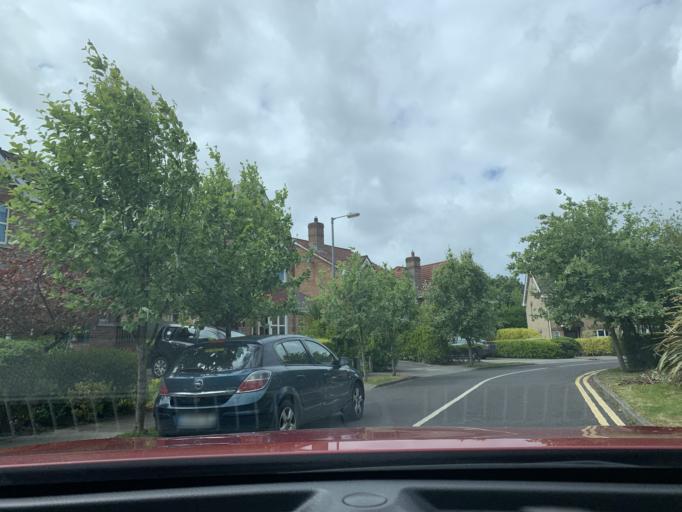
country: IE
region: Connaught
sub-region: Sligo
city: Sligo
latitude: 54.2739
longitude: -8.5128
